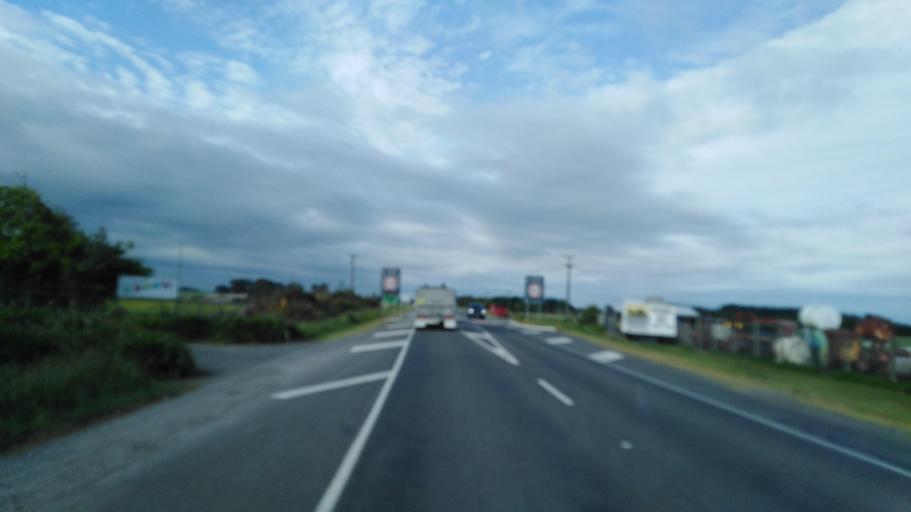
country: NZ
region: Manawatu-Wanganui
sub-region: Rangitikei District
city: Bulls
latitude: -40.2218
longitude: 175.4227
